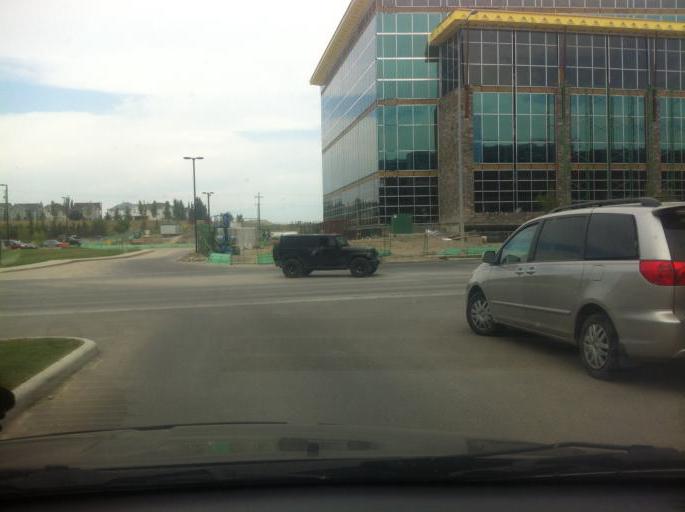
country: CA
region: Alberta
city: Calgary
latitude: 50.9631
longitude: -114.0048
